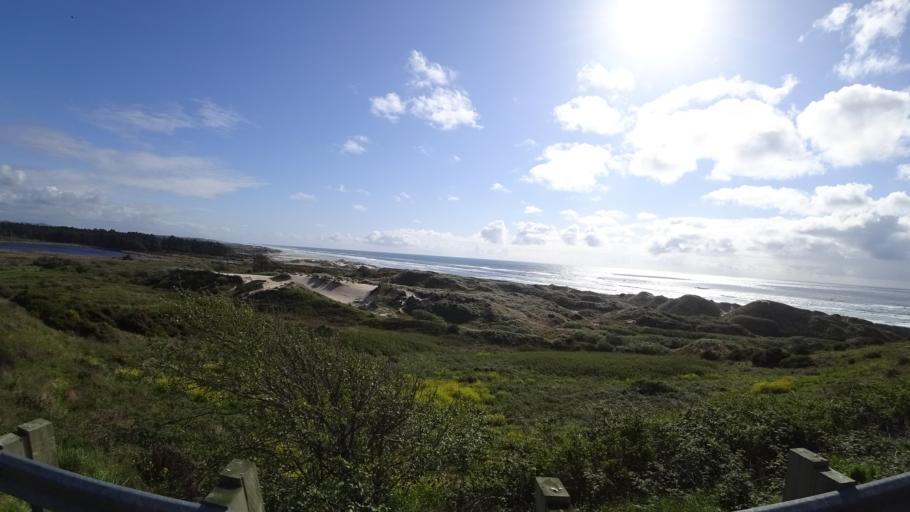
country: US
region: Oregon
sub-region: Lane County
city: Florence
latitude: 44.1001
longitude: -124.1194
